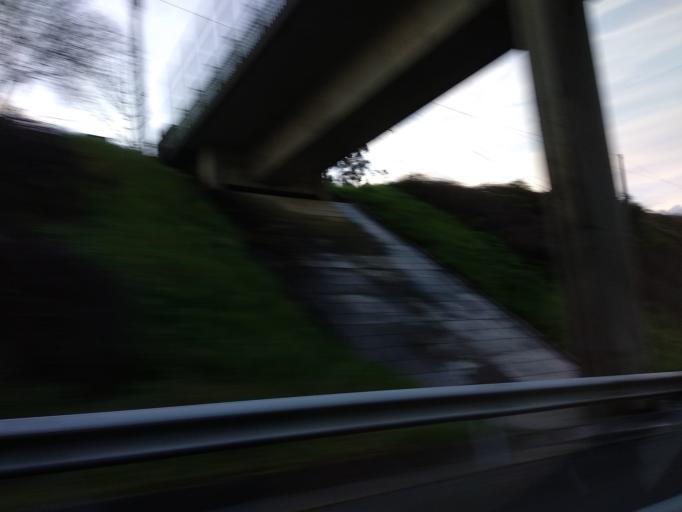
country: PT
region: Braga
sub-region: Braga
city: Oliveira
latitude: 41.4896
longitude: -8.4658
